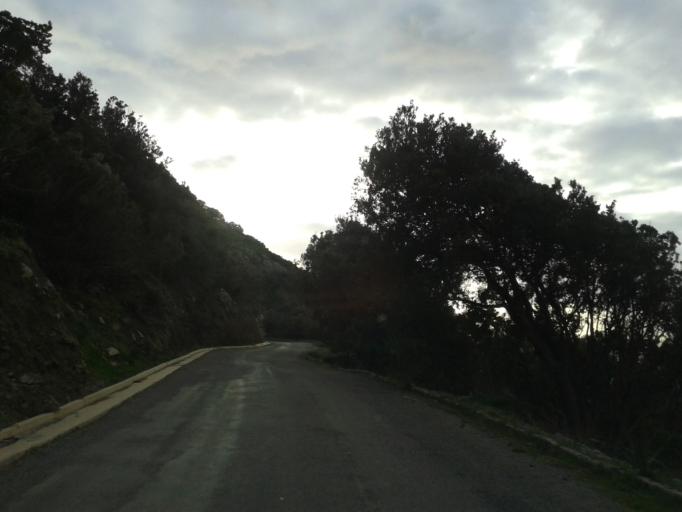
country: FR
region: Corsica
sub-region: Departement de la Haute-Corse
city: Brando
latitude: 42.8989
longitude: 9.3291
